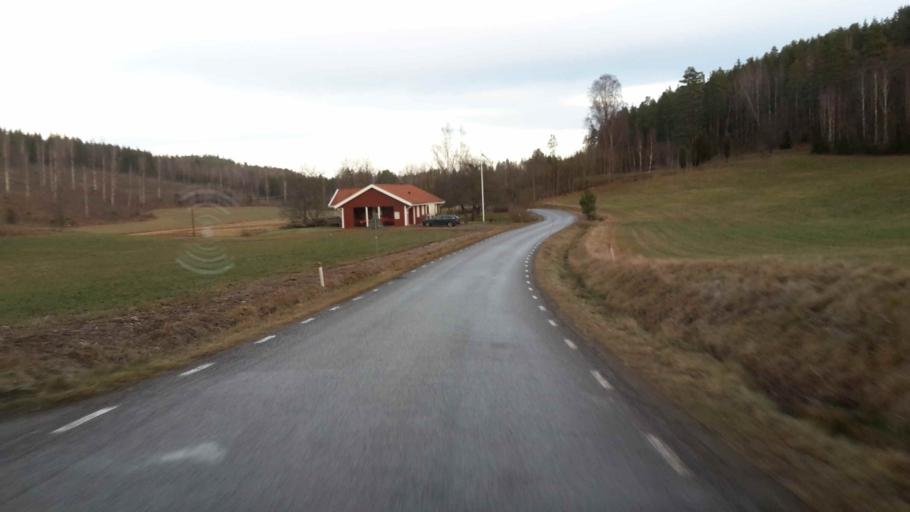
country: SE
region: Kalmar
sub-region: Vasterviks Kommun
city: Overum
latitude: 58.1595
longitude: 16.3310
